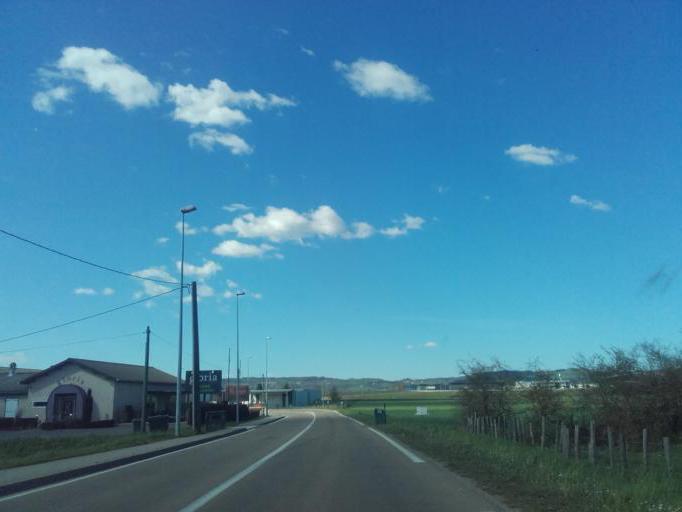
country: FR
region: Rhone-Alpes
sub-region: Departement de l'Isere
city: Saint-Etienne-de-Saint-Geoirs
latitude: 45.3492
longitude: 5.3380
